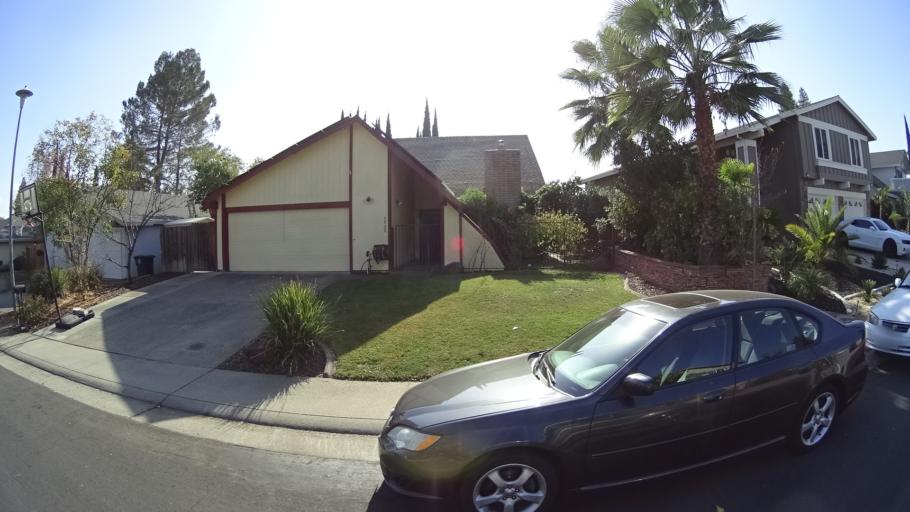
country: US
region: California
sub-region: Sacramento County
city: Citrus Heights
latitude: 38.6891
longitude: -121.2696
